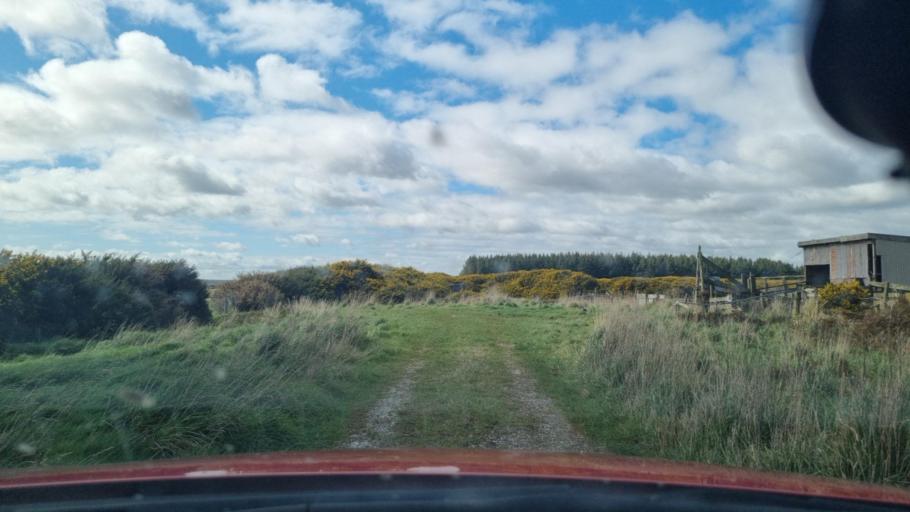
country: NZ
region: Southland
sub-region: Invercargill City
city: Invercargill
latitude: -46.4919
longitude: 168.4457
